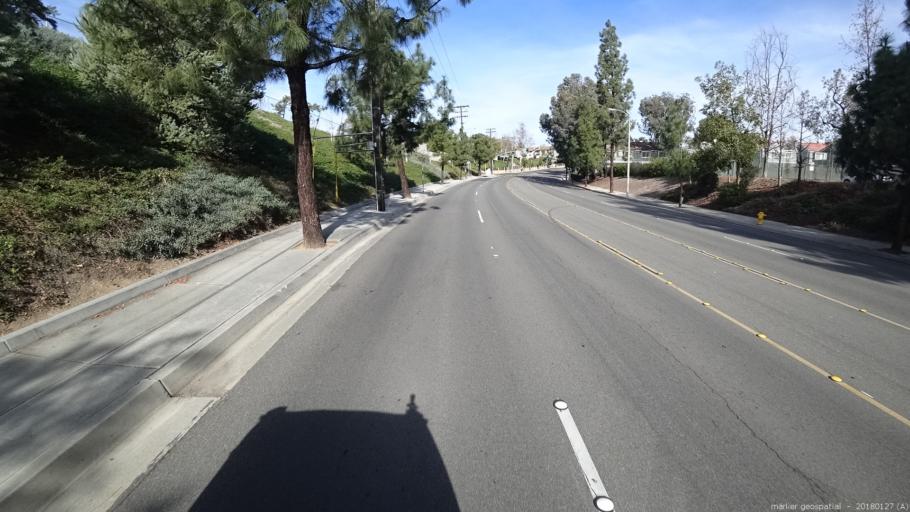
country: US
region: California
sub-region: Los Angeles County
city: Diamond Bar
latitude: 34.0320
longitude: -117.7972
